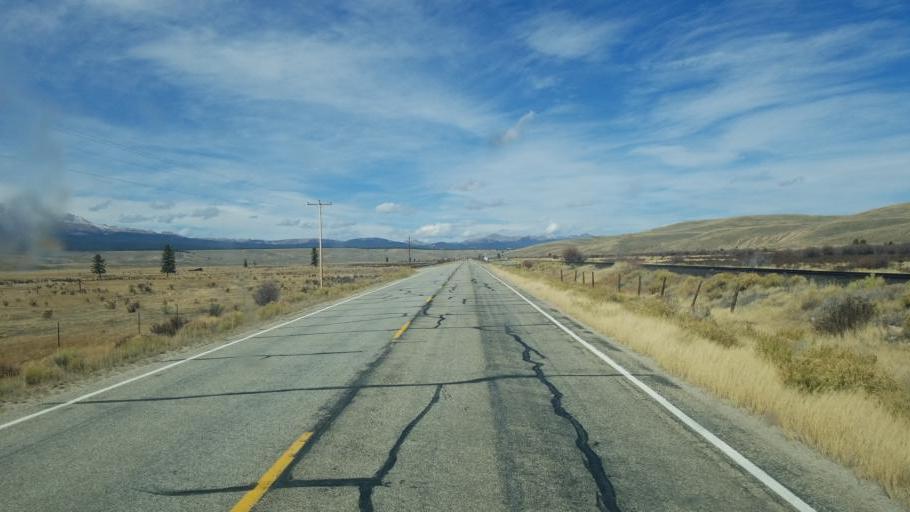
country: US
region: Colorado
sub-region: Lake County
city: Leadville
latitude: 39.1095
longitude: -106.3024
